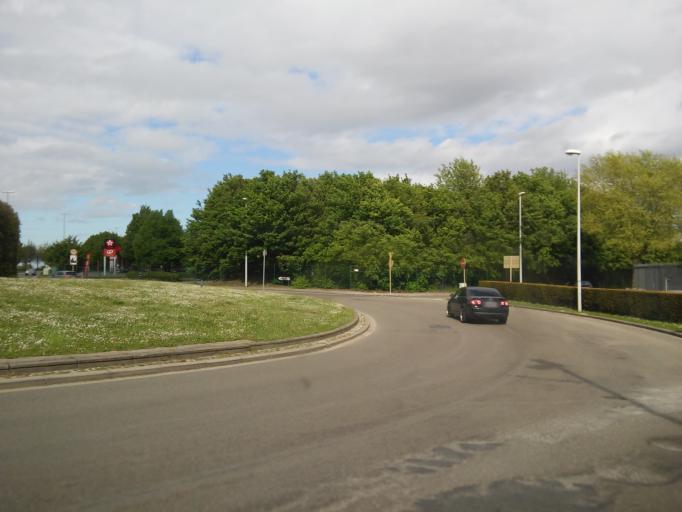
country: BE
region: Flanders
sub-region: Provincie Vlaams-Brabant
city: Dilbeek
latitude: 50.8152
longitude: 4.2619
